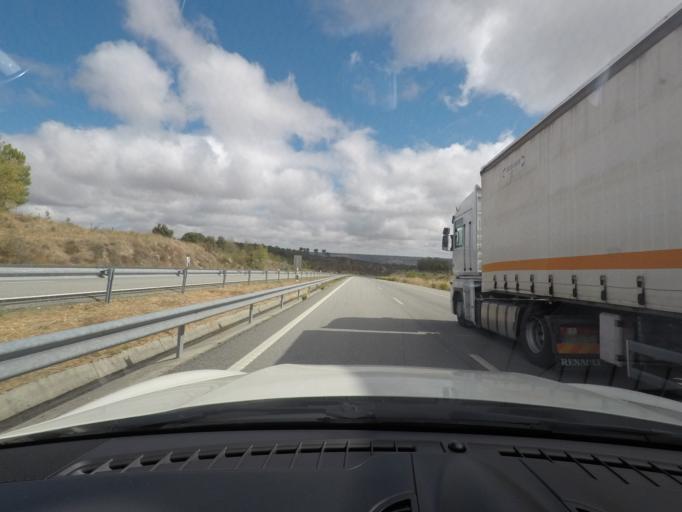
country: ES
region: Castille and Leon
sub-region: Provincia de Salamanca
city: Fuentes de Onoro
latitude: 40.6054
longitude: -6.9431
